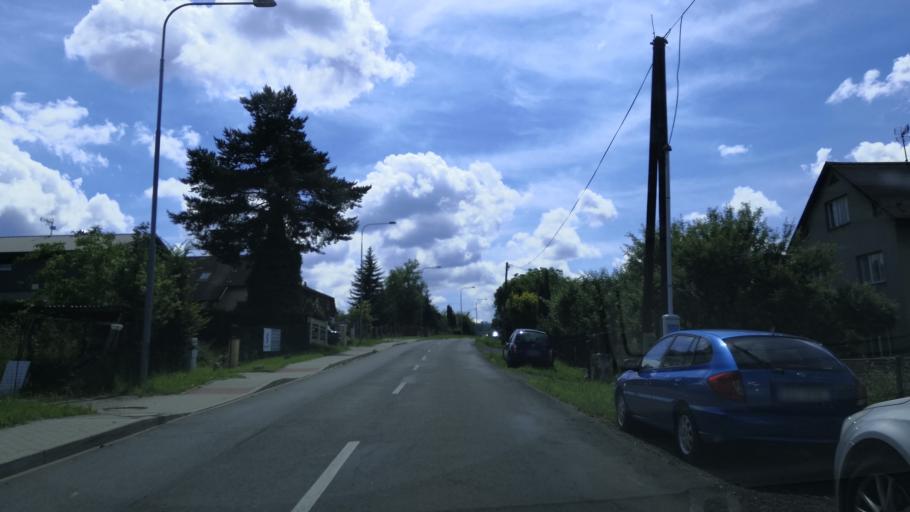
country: CZ
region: Zlin
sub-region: Okres Vsetin
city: Roznov pod Radhostem
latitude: 49.4516
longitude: 18.1425
